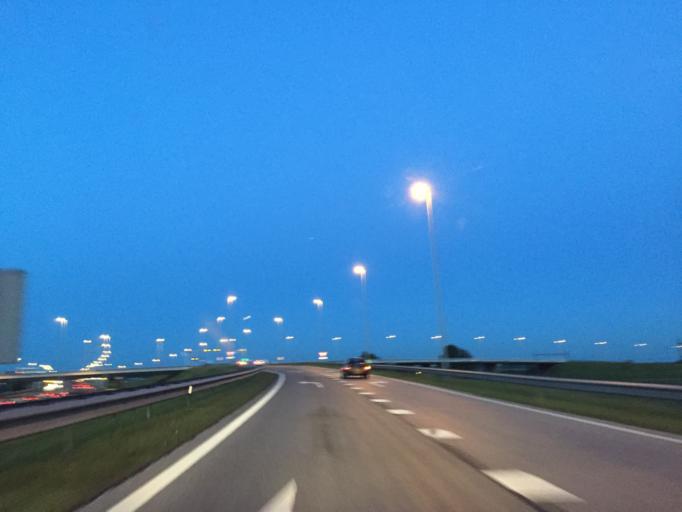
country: NL
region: South Holland
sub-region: Gemeente Waddinxveen
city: Groenswaard
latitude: 52.0197
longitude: 4.6063
